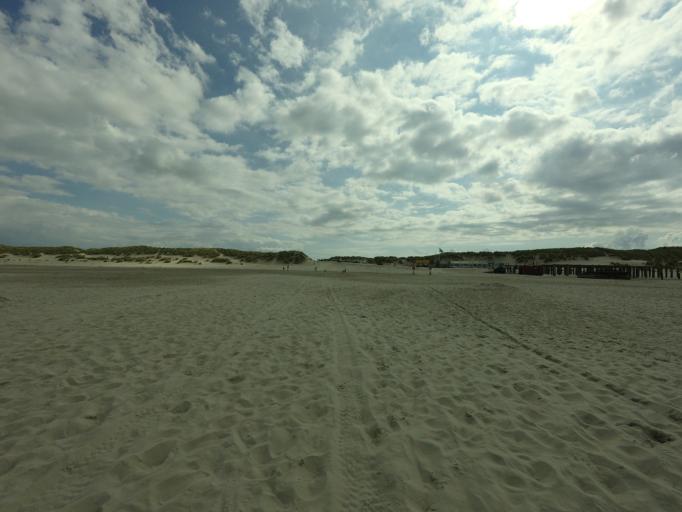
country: NL
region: Friesland
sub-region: Gemeente Terschelling
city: West-Terschelling
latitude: 53.4028
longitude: 5.2513
